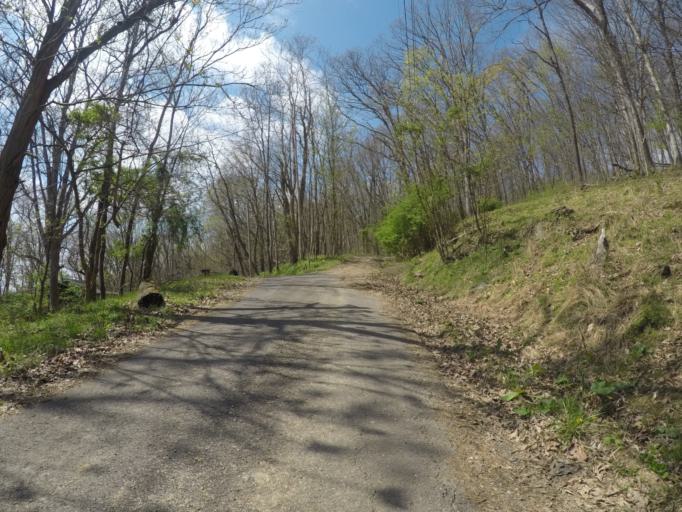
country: US
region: Ohio
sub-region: Lawrence County
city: Burlington
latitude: 38.3870
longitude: -82.5189
